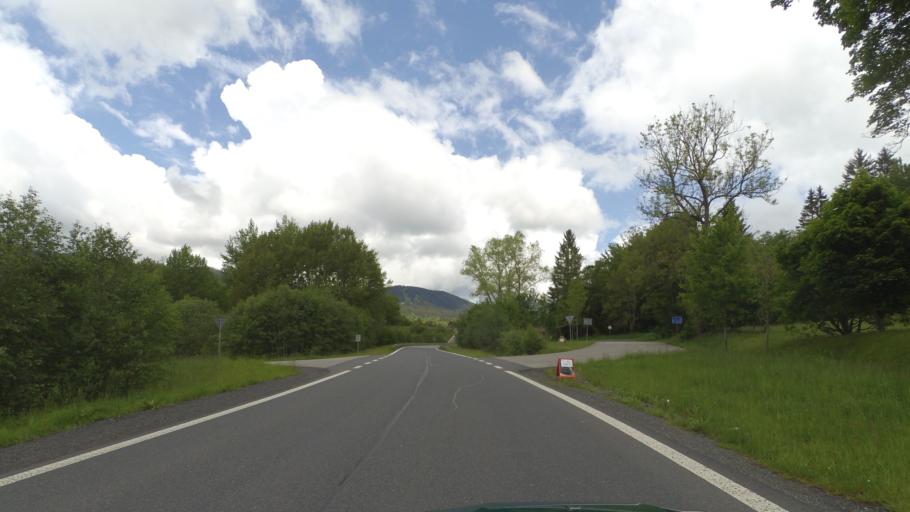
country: CZ
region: Plzensky
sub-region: Okres Klatovy
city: Zelezna Ruda
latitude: 49.1459
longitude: 13.2278
